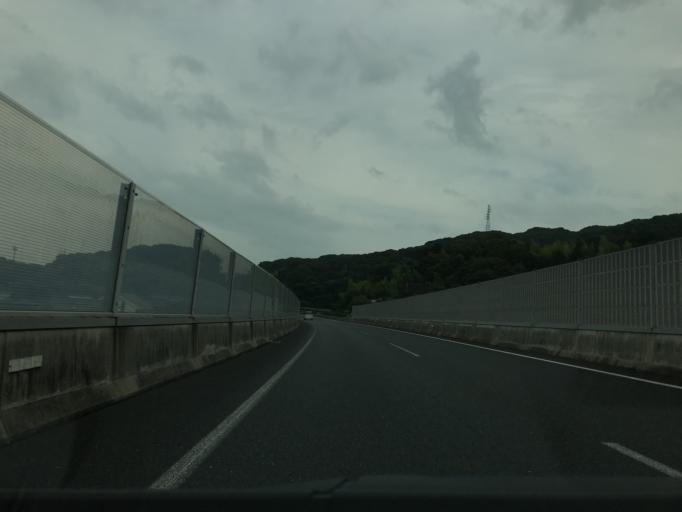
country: JP
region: Fukuoka
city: Kanda
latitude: 33.8007
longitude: 130.9514
